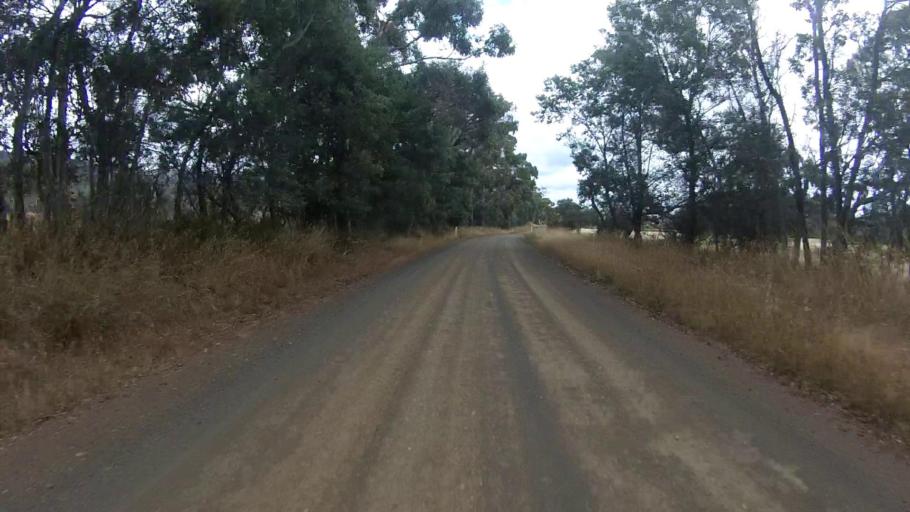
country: AU
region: Tasmania
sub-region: Break O'Day
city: St Helens
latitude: -41.8257
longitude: 147.9818
